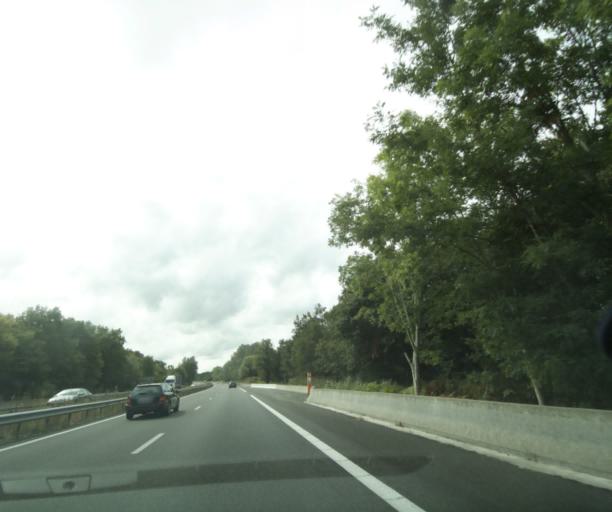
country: FR
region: Poitou-Charentes
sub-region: Departement de la Charente-Maritime
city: Saint-Genis-de-Saintonge
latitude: 45.4782
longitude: -0.6196
